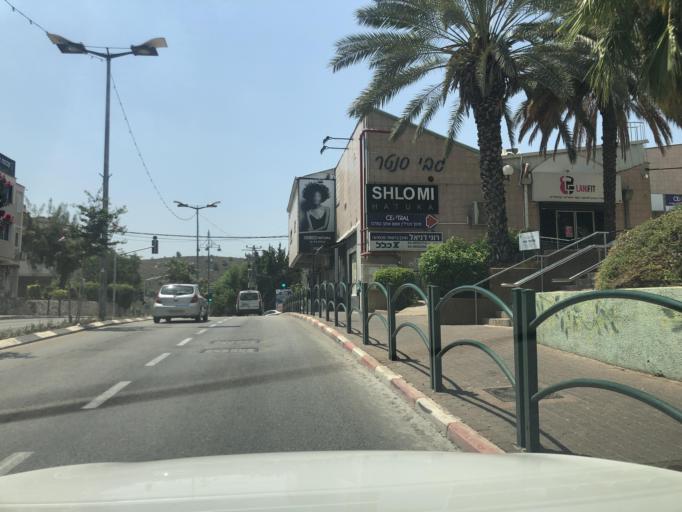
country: IL
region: Haifa
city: Daliyat el Karmil
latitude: 32.6550
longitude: 35.1050
